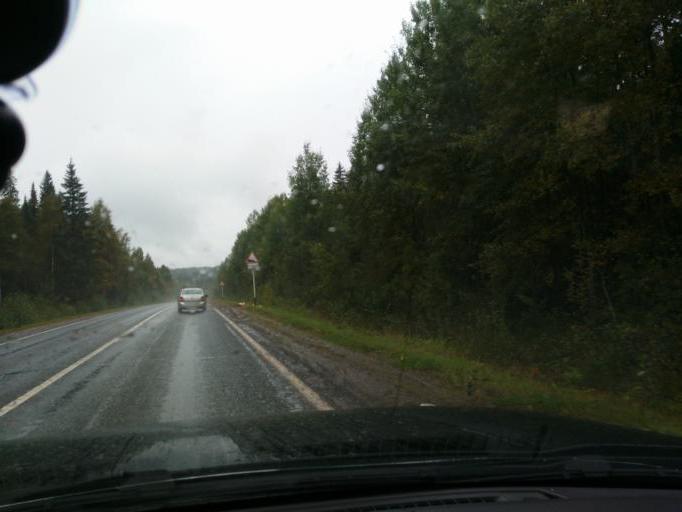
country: RU
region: Perm
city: Yugo-Kamskiy
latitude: 57.6108
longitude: 55.6404
